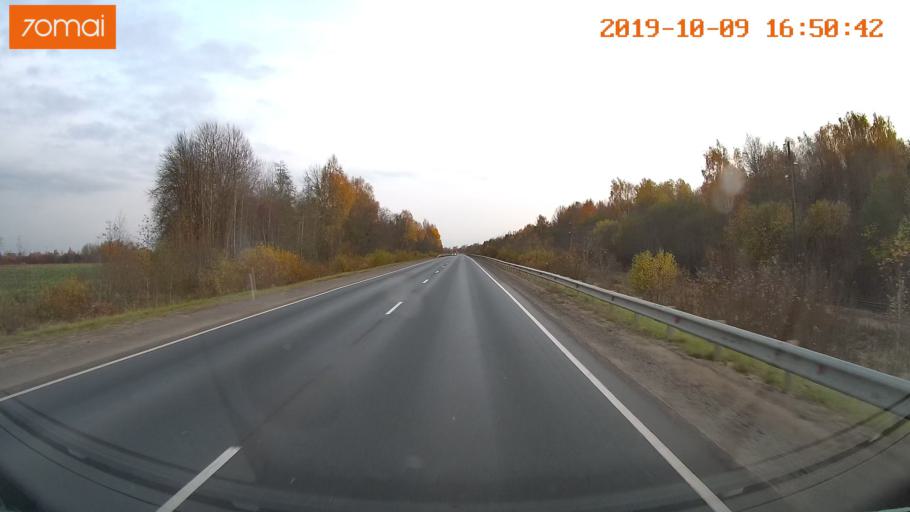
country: RU
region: Kostroma
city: Volgorechensk
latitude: 57.3973
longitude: 41.2122
